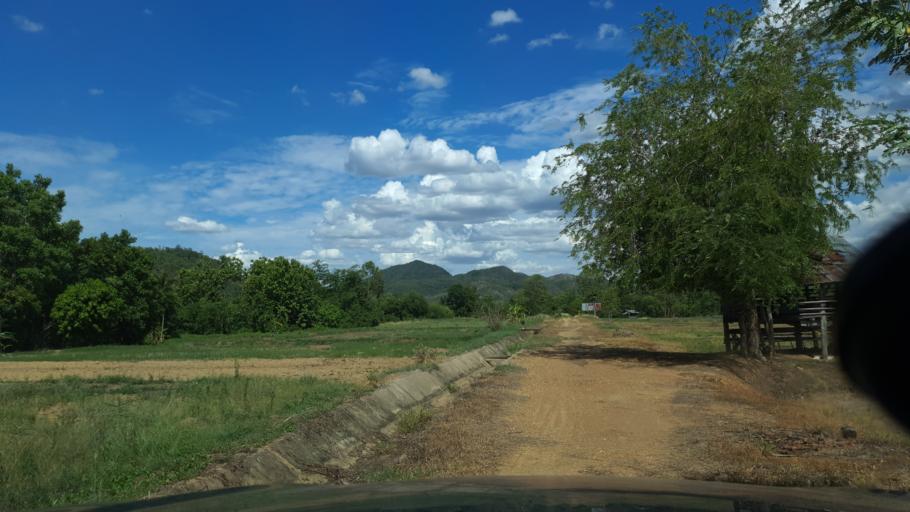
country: TH
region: Sukhothai
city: Thung Saliam
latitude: 17.3386
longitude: 99.4417
